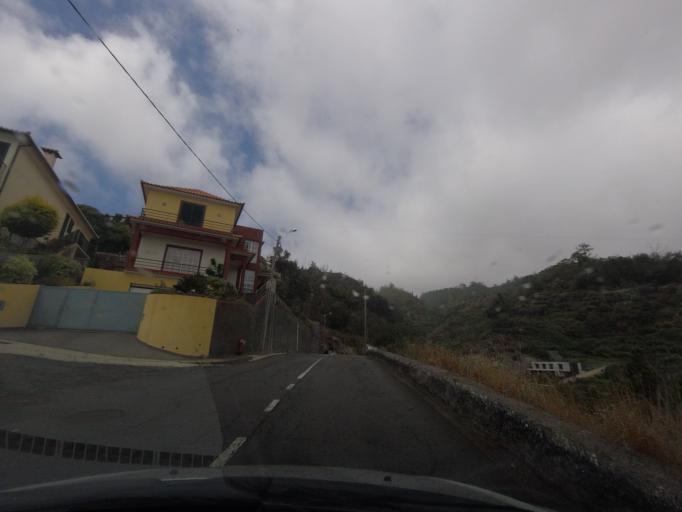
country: PT
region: Madeira
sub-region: Machico
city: Machico
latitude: 32.7057
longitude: -16.7773
